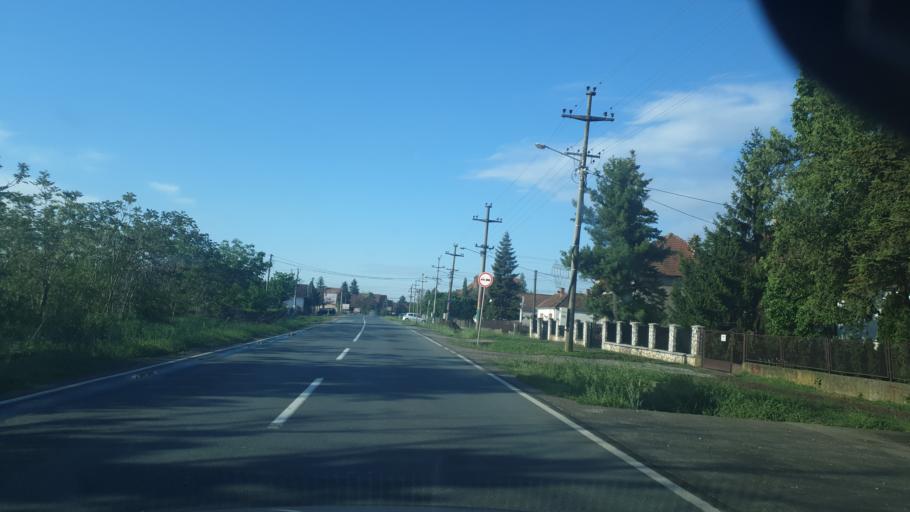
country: RS
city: Zvecka
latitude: 44.6338
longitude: 20.1816
